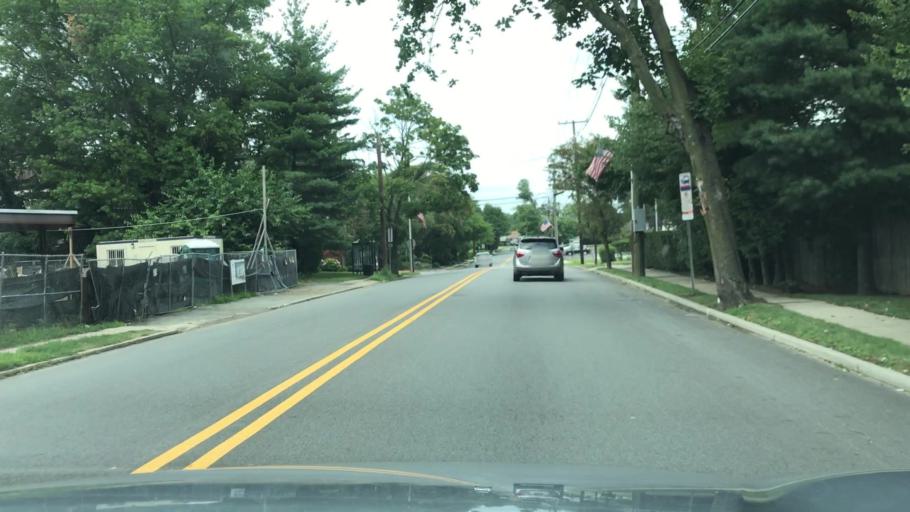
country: US
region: New Jersey
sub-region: Bergen County
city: River Edge
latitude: 40.9185
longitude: -74.0262
